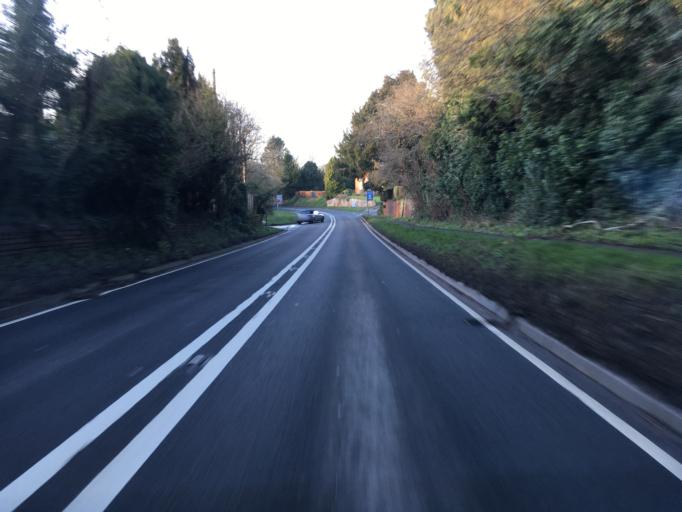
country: GB
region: England
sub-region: Warwickshire
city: Henley in Arden
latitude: 52.2649
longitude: -1.7691
